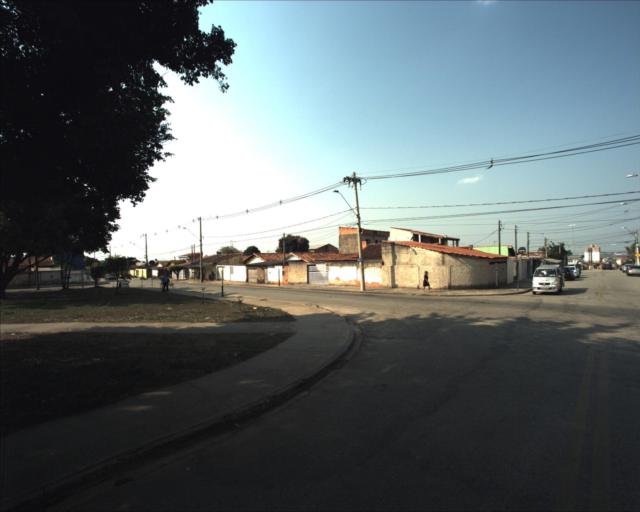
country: BR
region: Sao Paulo
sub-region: Sorocaba
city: Sorocaba
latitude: -23.4368
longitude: -47.4749
